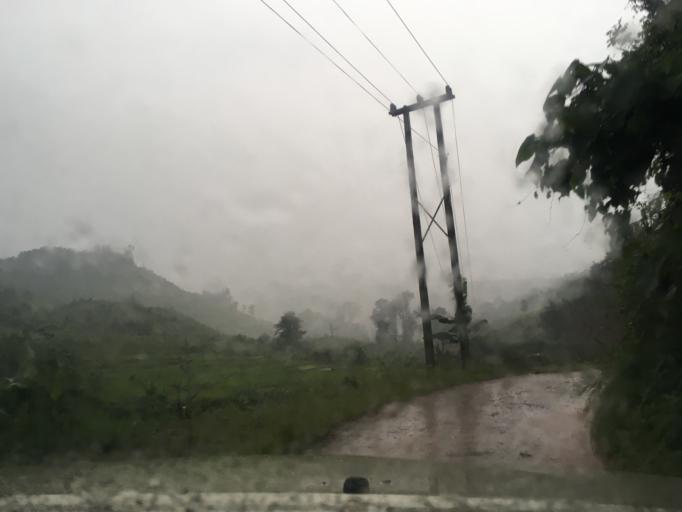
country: LA
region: Oudomxai
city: Muang La
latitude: 21.2321
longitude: 101.9591
